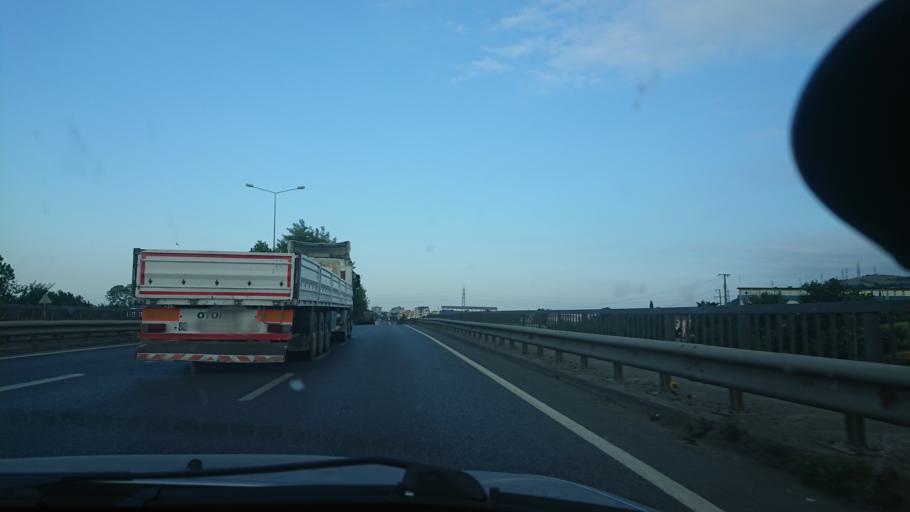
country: TR
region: Samsun
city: Tekkekoy
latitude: 41.2252
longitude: 36.4323
